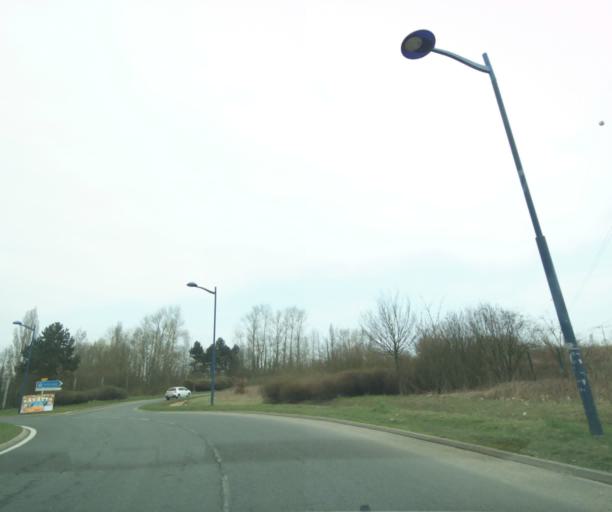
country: FR
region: Ile-de-France
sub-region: Departement du Val-d'Oise
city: Courdimanche
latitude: 49.0536
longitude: 2.0035
